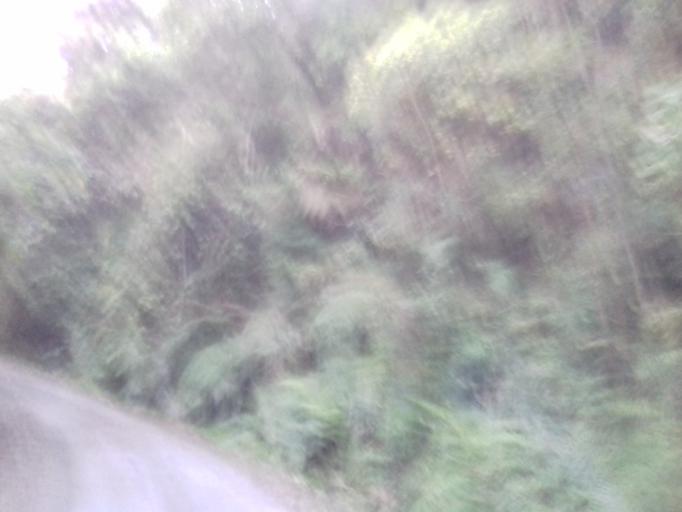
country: CO
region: Quindio
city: Salento
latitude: 4.5537
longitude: -75.4999
